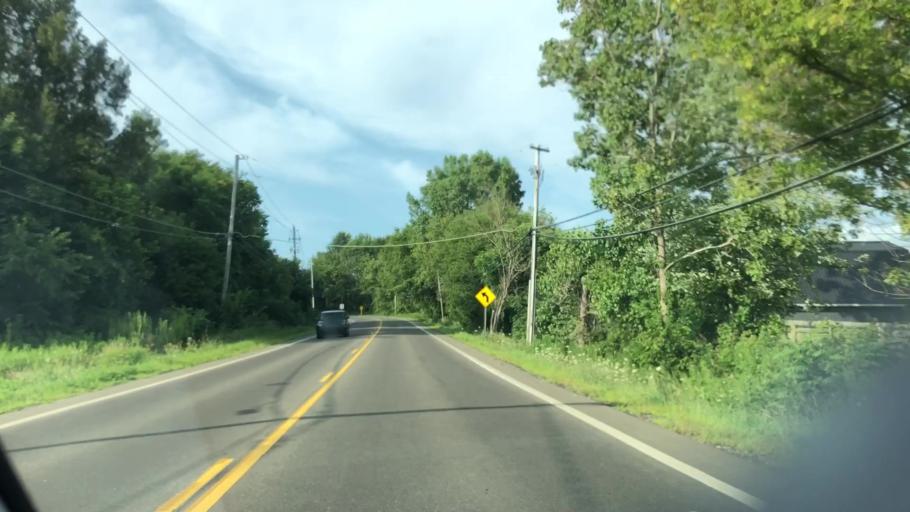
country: US
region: Ohio
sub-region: Summit County
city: Greensburg
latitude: 40.8684
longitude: -81.4814
